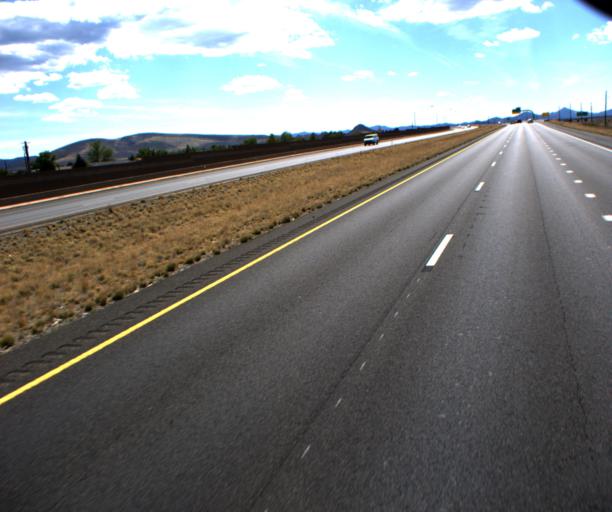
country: US
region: Arizona
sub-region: Yavapai County
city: Prescott Valley
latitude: 34.6392
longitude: -112.3237
